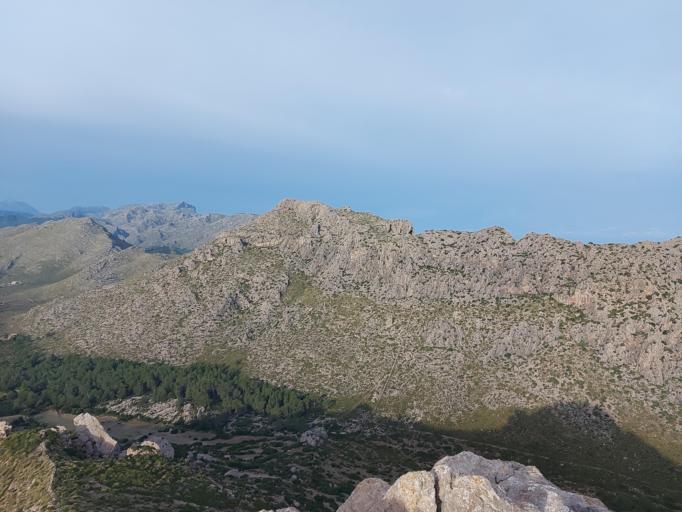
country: ES
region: Balearic Islands
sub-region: Illes Balears
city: Alcudia
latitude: 39.9185
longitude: 3.0881
